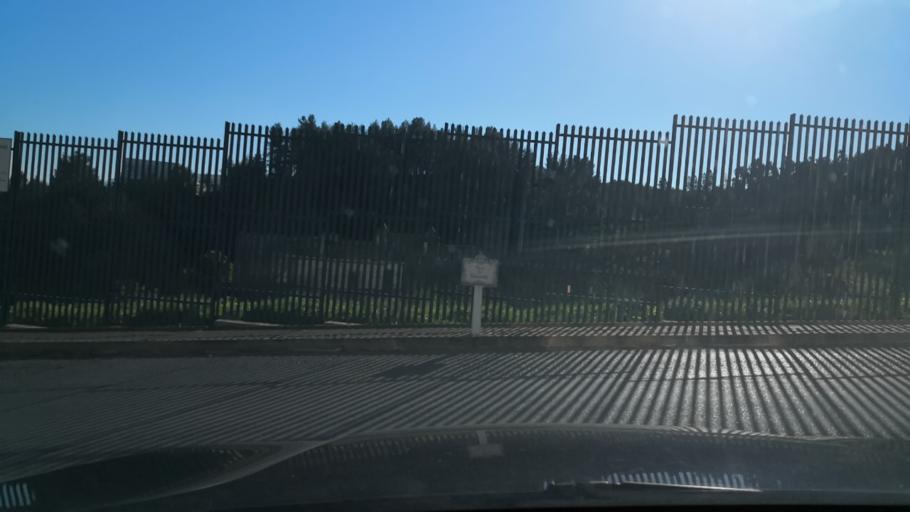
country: PT
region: Setubal
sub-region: Setubal
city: Setubal
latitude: 38.5239
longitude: -8.9063
